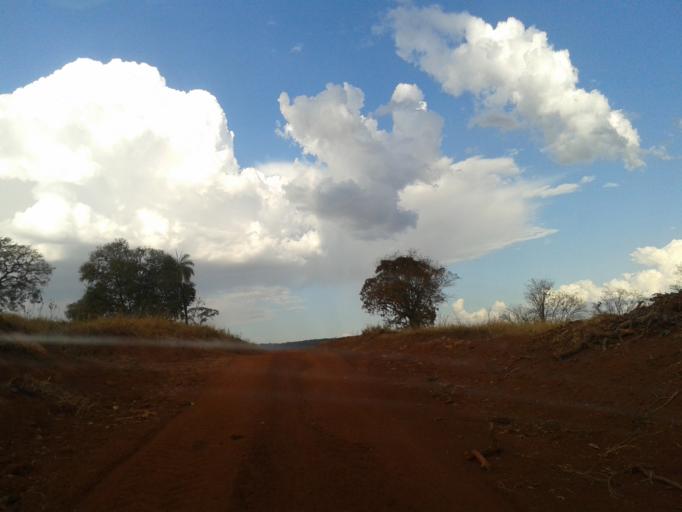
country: BR
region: Minas Gerais
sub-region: Santa Vitoria
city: Santa Vitoria
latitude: -19.1707
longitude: -49.9447
